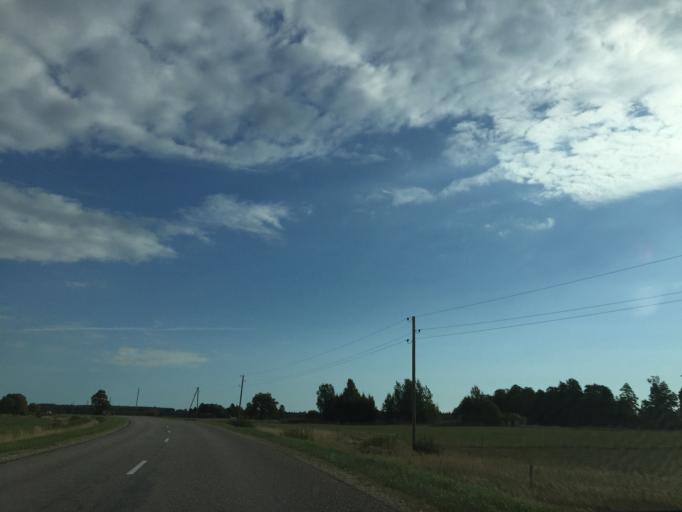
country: LV
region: Limbazu Rajons
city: Limbazi
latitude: 57.5044
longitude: 24.4970
